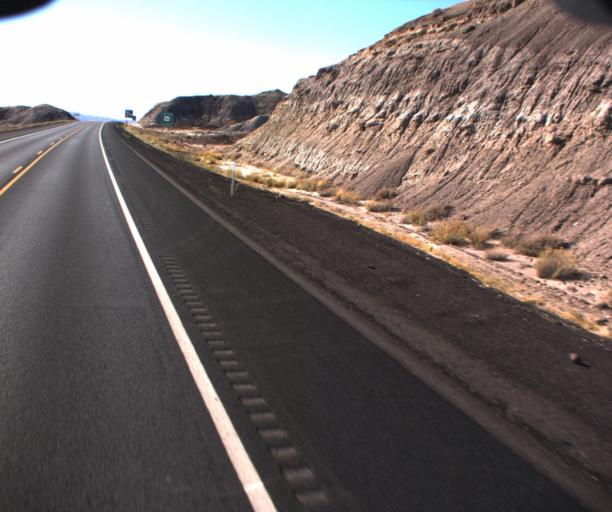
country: US
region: Arizona
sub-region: Coconino County
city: Tuba City
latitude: 36.0836
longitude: -111.3919
